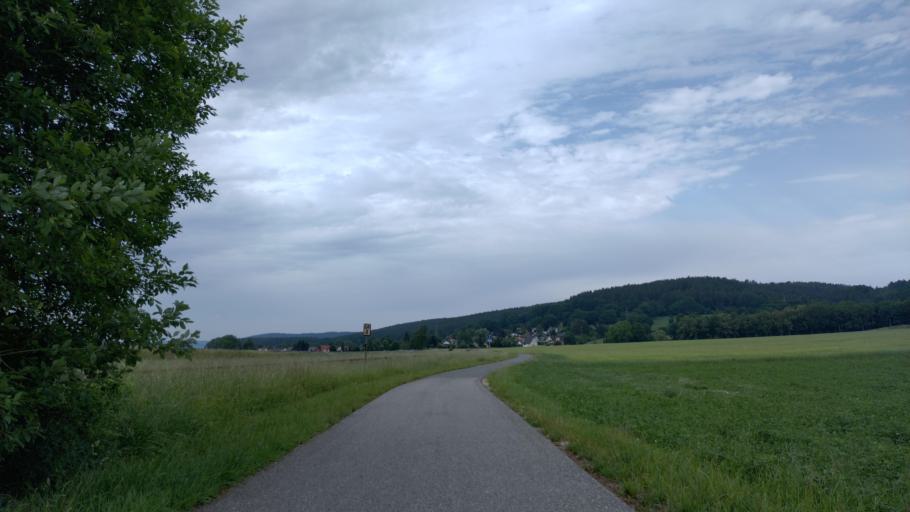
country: DE
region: Bavaria
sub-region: Upper Franconia
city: Bindlach
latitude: 49.9994
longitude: 11.6018
